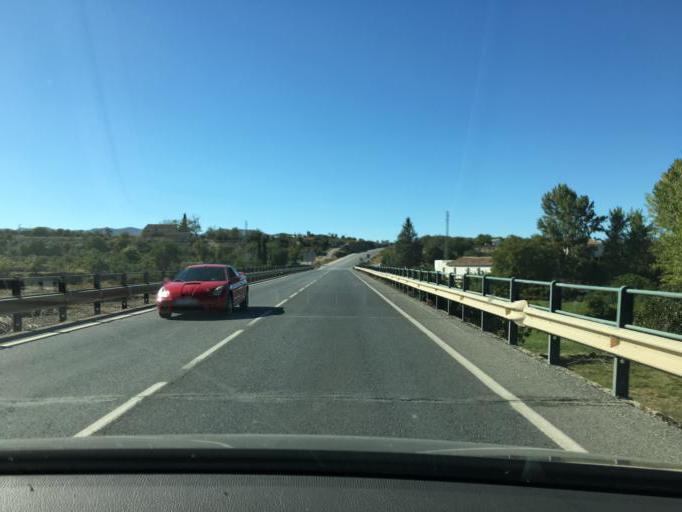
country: ES
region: Andalusia
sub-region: Provincia de Granada
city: Caniles
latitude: 37.4469
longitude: -2.7269
